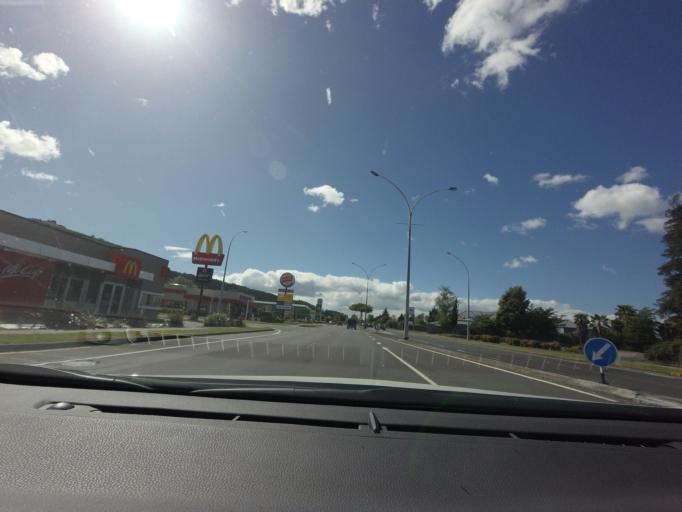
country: NZ
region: Bay of Plenty
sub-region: Rotorua District
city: Rotorua
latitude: -38.1185
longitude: 176.2278
